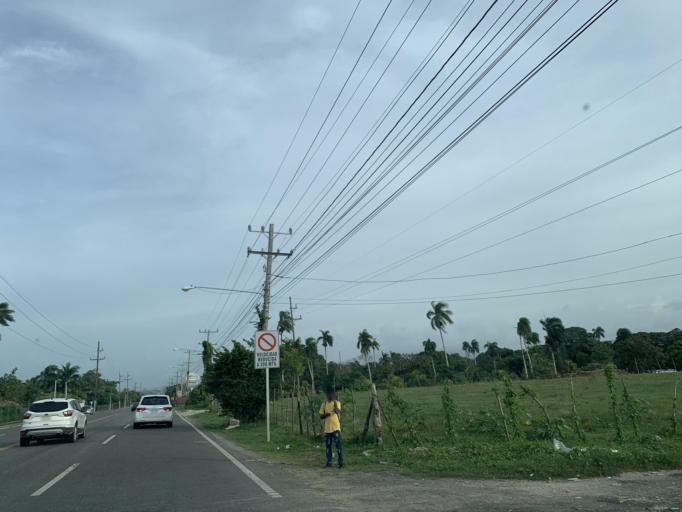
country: DO
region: Puerto Plata
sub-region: Puerto Plata
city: Puerto Plata
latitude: 19.7578
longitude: -70.6449
